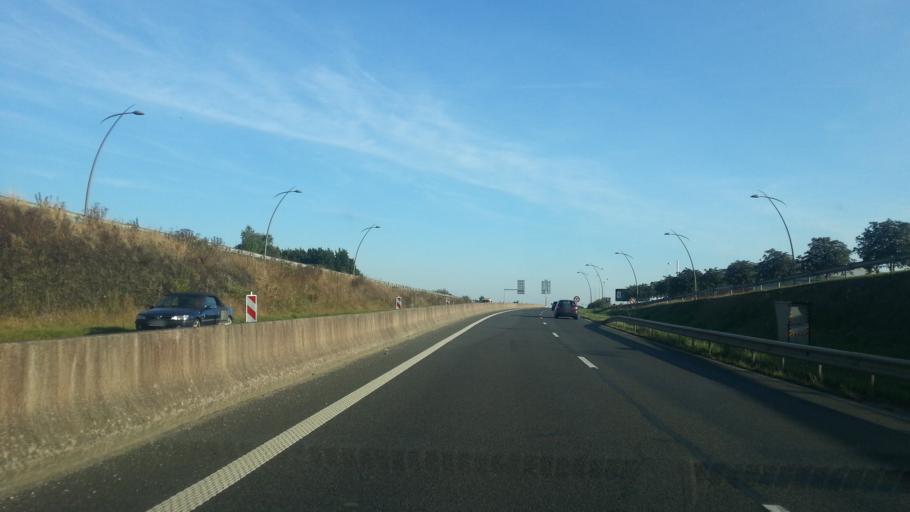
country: FR
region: Picardie
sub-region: Departement de l'Oise
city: Tille
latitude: 49.4521
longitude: 2.0997
